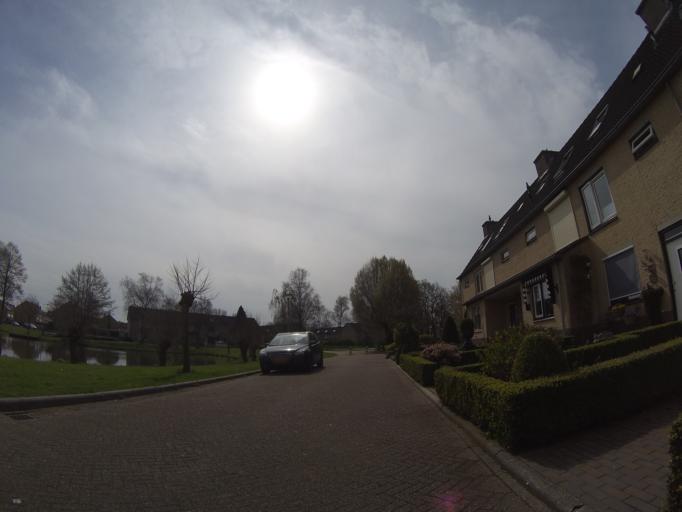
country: NL
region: Gelderland
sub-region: Gemeente Barneveld
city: Barneveld
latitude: 52.1511
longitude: 5.5847
